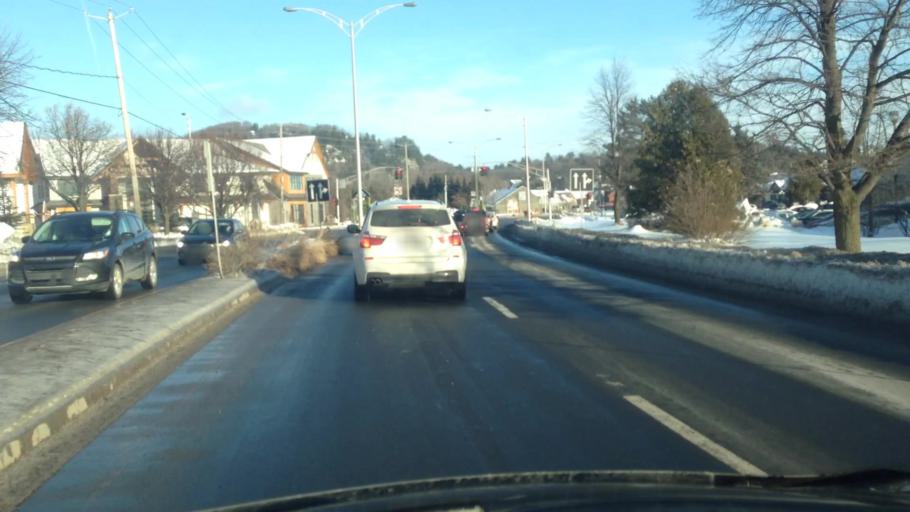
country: CA
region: Quebec
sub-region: Laurentides
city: Saint-Sauveur
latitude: 45.8921
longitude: -74.1559
